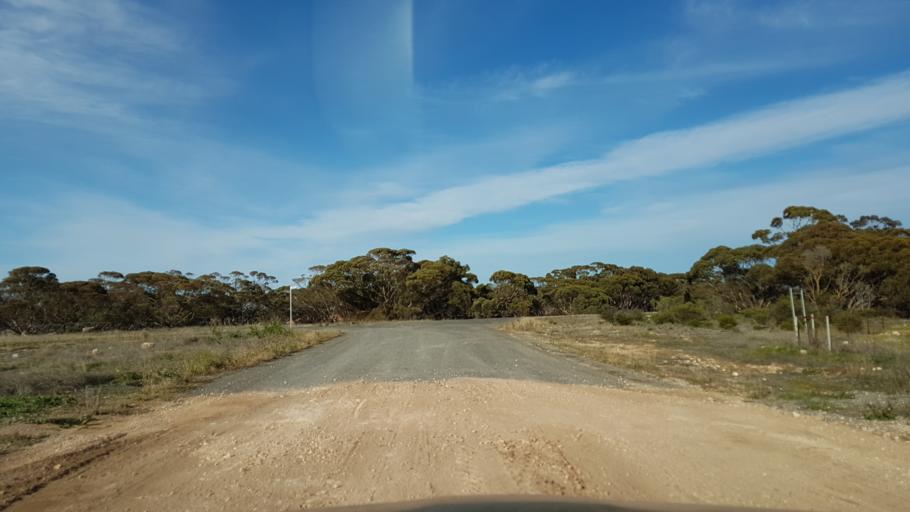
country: AU
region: South Australia
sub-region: Mid Murray
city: Mannum
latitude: -34.9850
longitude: 139.5737
